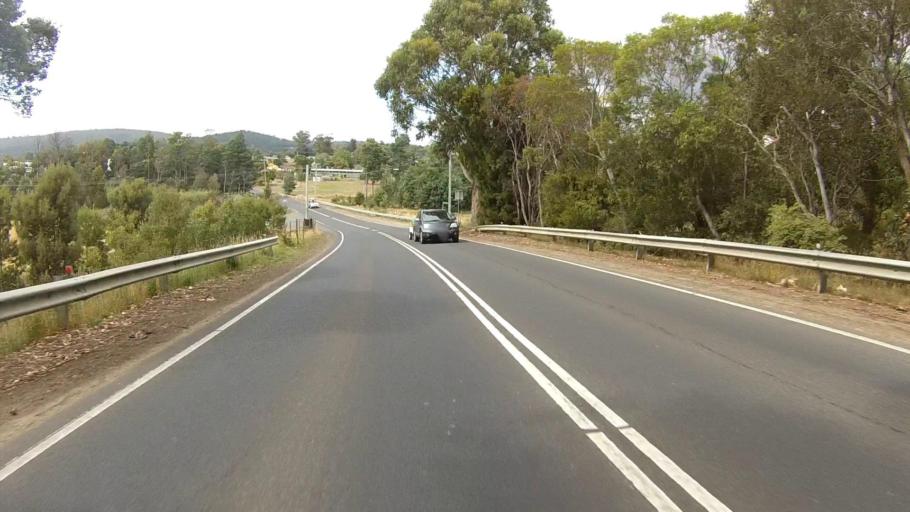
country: AU
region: Tasmania
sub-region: Kingborough
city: Margate
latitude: -43.0626
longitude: 147.2535
